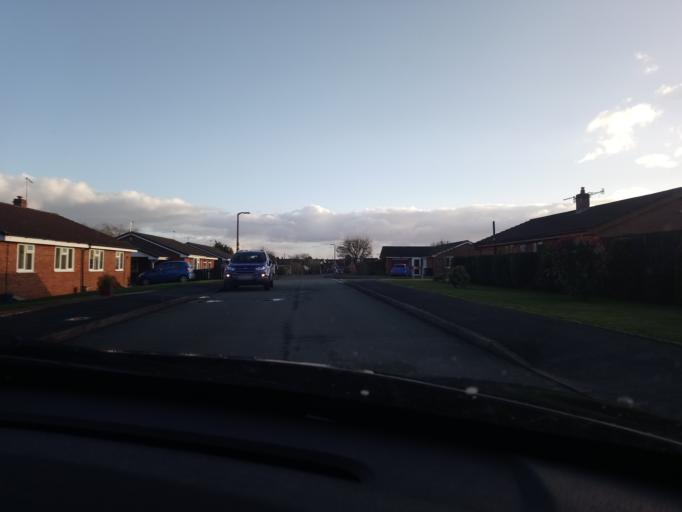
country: GB
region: England
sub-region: Shropshire
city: Wem
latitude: 52.8618
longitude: -2.7264
